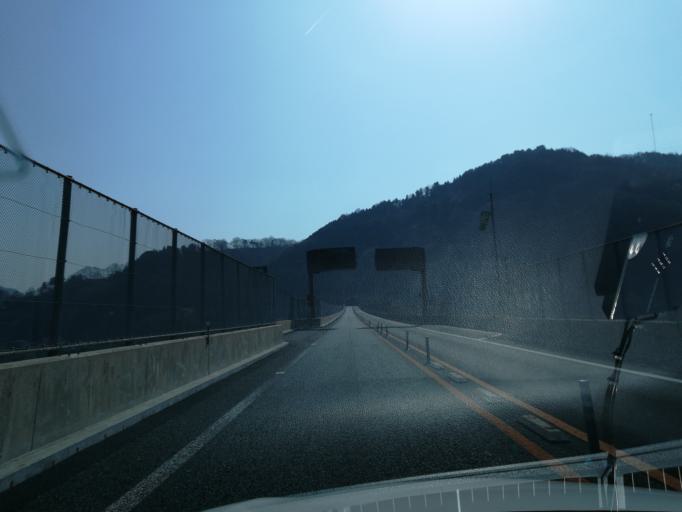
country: JP
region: Tokushima
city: Ikedacho
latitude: 34.0247
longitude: 133.7846
